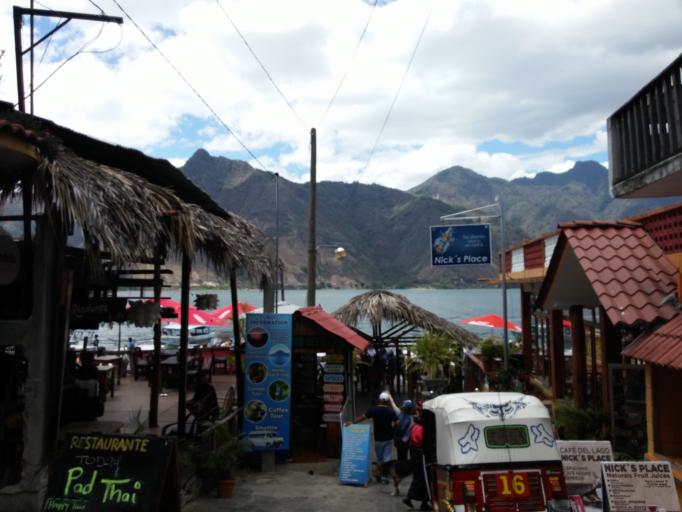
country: GT
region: Solola
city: San Pedro La Laguna
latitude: 14.6948
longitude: -91.2737
